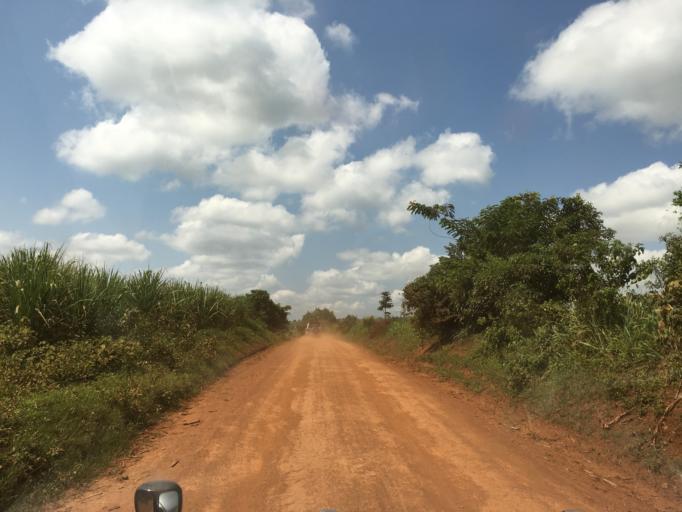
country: UG
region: Western Region
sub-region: Masindi District
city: Masindi
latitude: 1.5287
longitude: 31.5554
